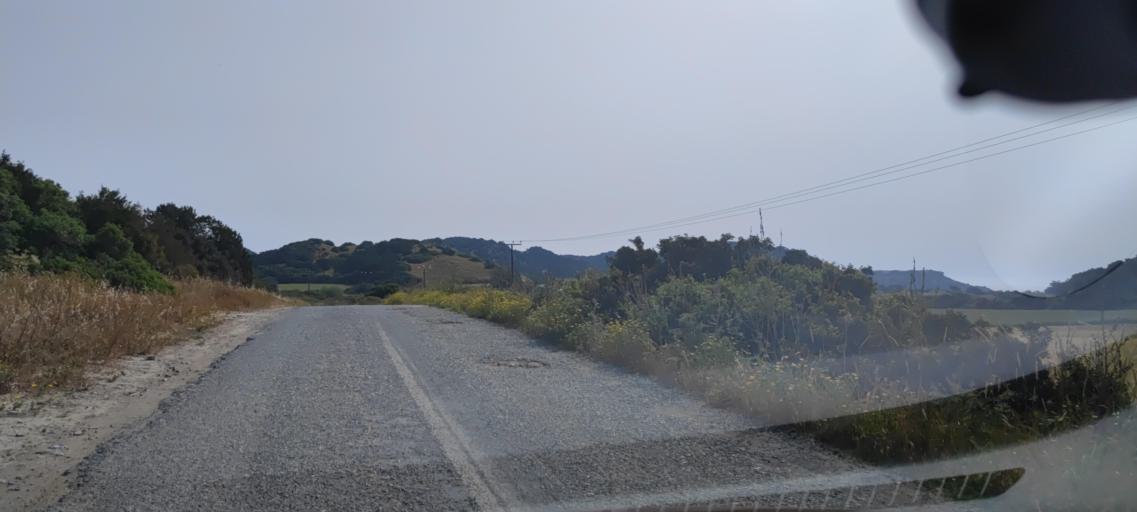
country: CY
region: Ammochostos
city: Rizokarpaso
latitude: 35.6290
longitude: 34.4925
